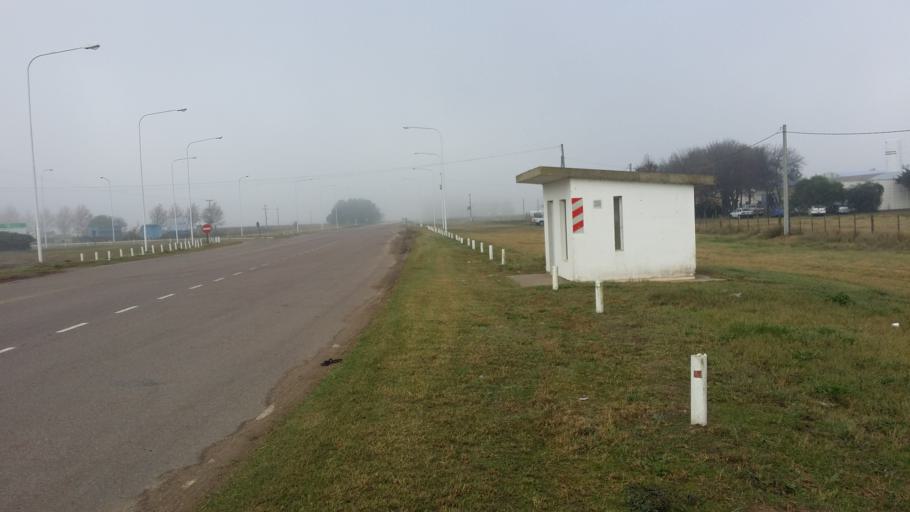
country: AR
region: La Pampa
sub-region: Departamento de Quemu Quemu
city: Quemu Quemu
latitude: -36.0635
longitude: -63.5853
